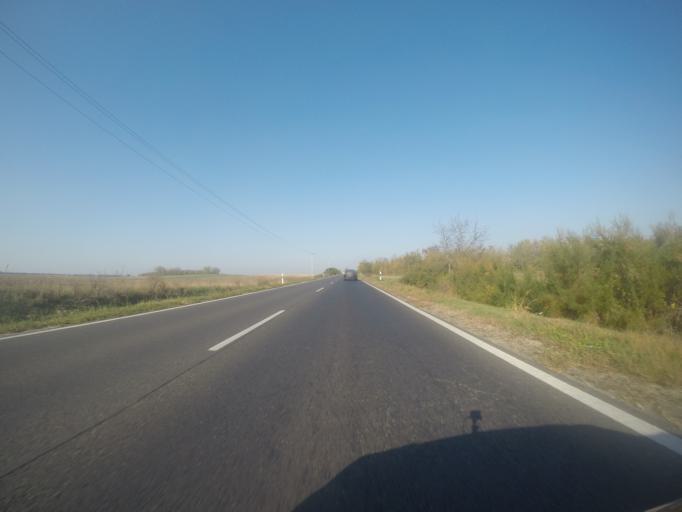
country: HU
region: Fejer
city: Baracs
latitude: 46.8557
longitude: 18.9130
